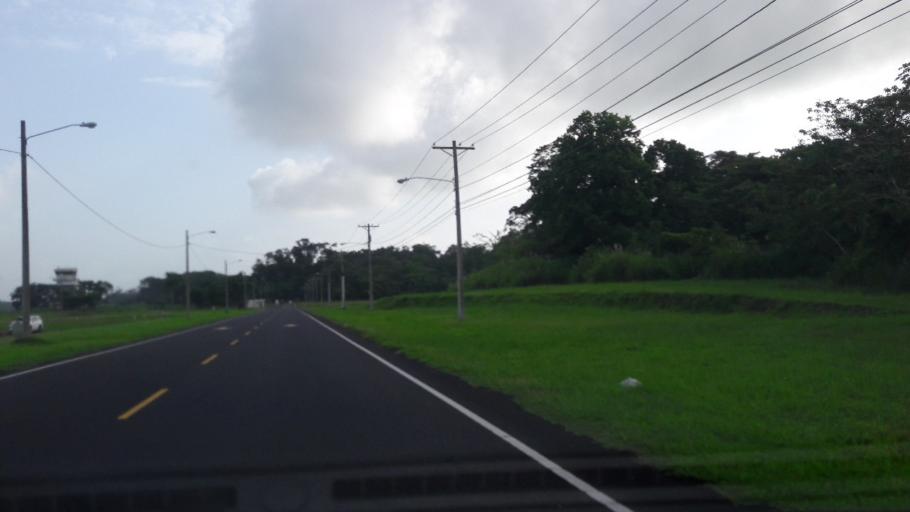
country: PA
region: Colon
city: Cativa
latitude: 9.3594
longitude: -79.8631
